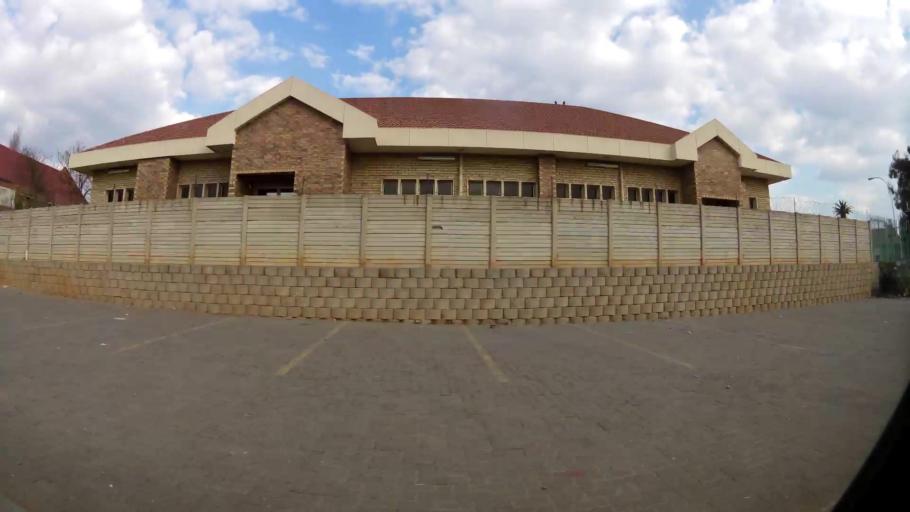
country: ZA
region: Gauteng
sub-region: City of Johannesburg Metropolitan Municipality
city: Soweto
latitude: -26.2253
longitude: 27.9329
